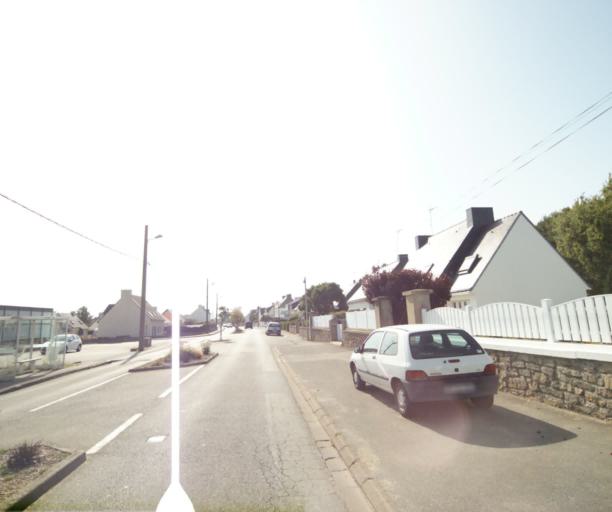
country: FR
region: Brittany
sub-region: Departement du Morbihan
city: Riantec
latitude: 47.7128
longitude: -3.3206
